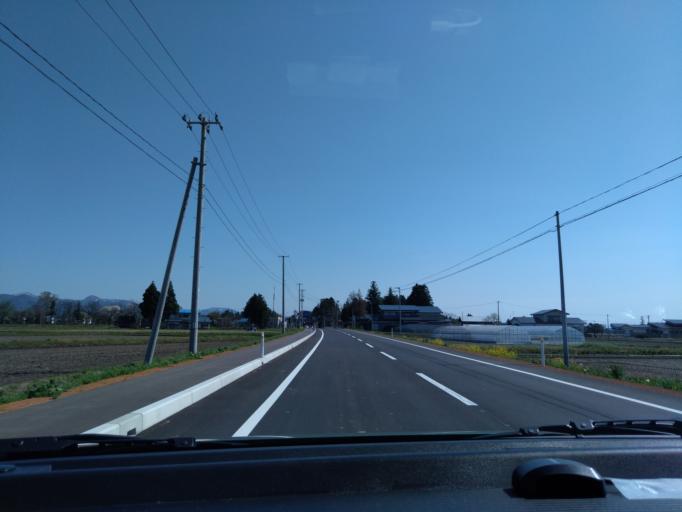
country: JP
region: Akita
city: Kakunodatemachi
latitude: 39.5350
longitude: 140.5852
